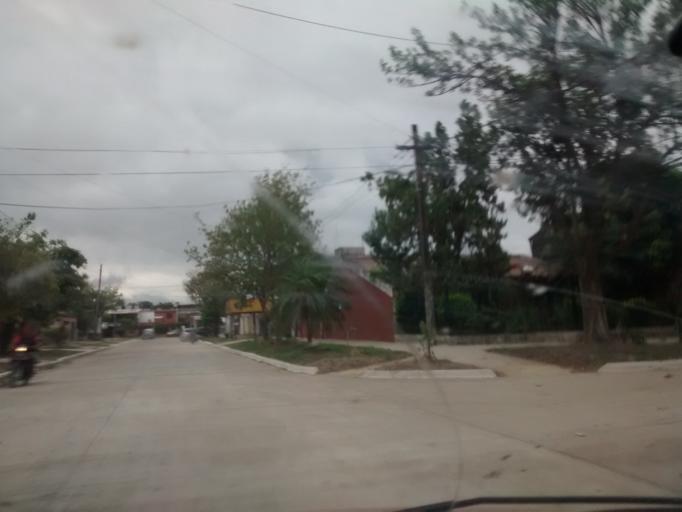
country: AR
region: Chaco
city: Resistencia
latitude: -27.4500
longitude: -59.0120
